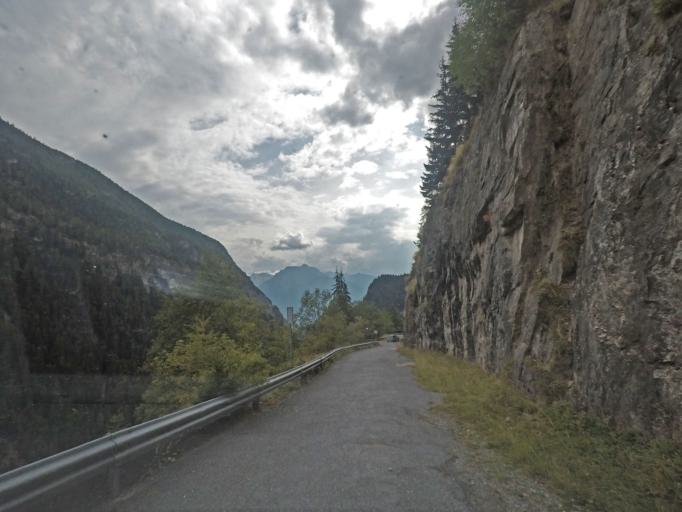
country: CH
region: Valais
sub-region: Brig District
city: Naters
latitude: 46.3692
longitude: 7.9998
